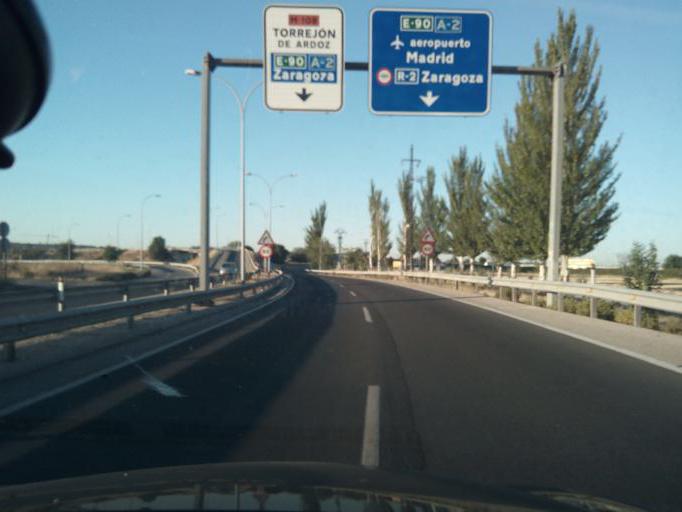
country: ES
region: Madrid
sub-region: Provincia de Madrid
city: Torrejon de Ardoz
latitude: 40.4690
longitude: -3.4852
